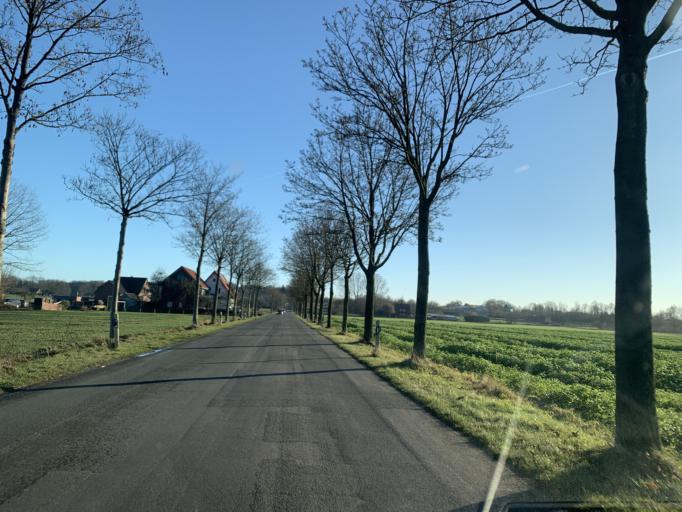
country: DE
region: North Rhine-Westphalia
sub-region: Regierungsbezirk Munster
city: Dulmen
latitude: 51.8499
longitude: 7.2927
